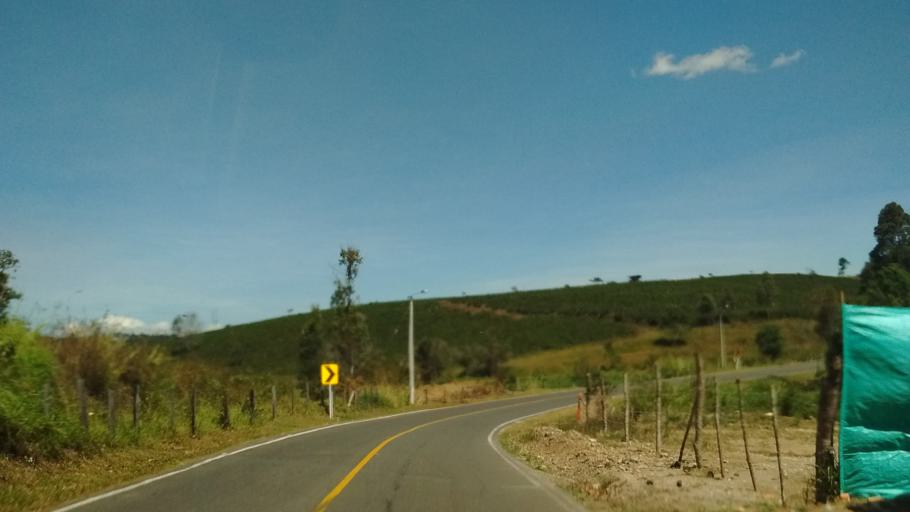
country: CO
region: Cauca
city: Popayan
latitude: 2.3620
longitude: -76.6861
